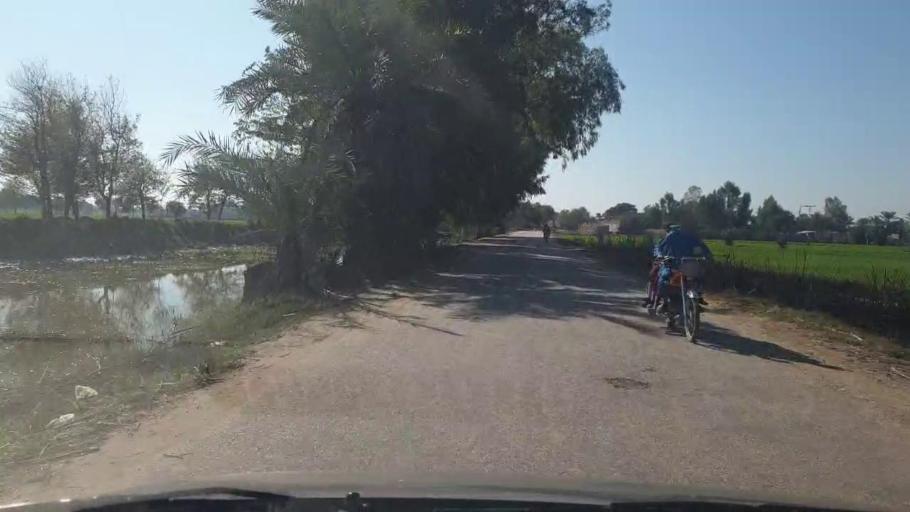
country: PK
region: Sindh
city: Bozdar
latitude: 27.0981
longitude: 68.6288
